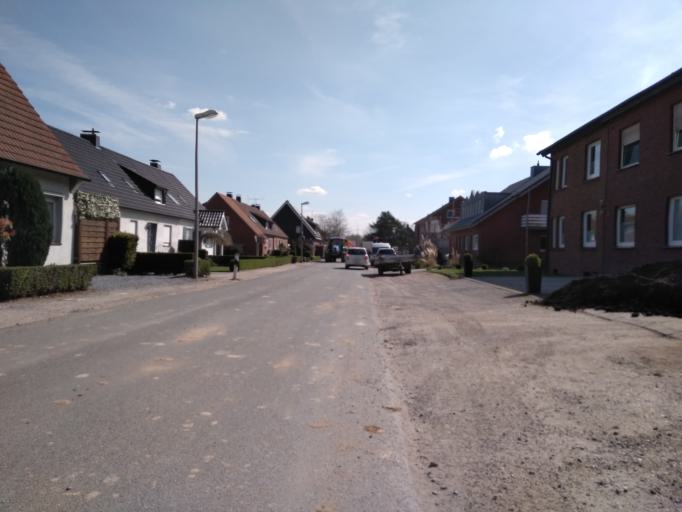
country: DE
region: North Rhine-Westphalia
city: Dorsten
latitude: 51.6518
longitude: 6.9259
